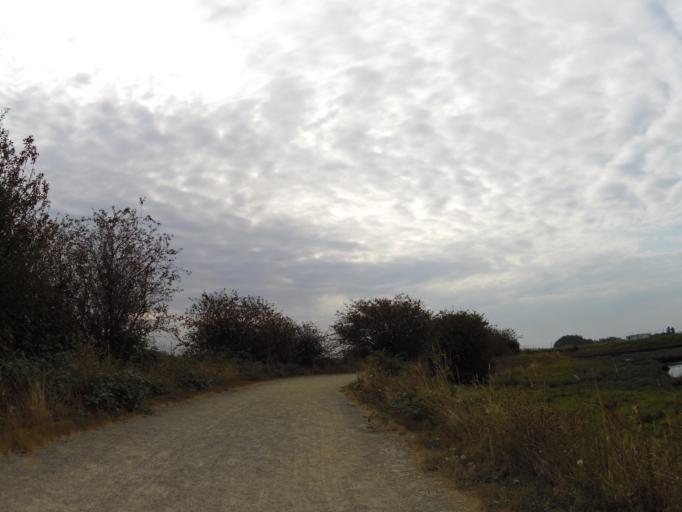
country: US
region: Washington
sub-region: Skagit County
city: Mount Vernon
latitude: 48.4578
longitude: -122.4689
